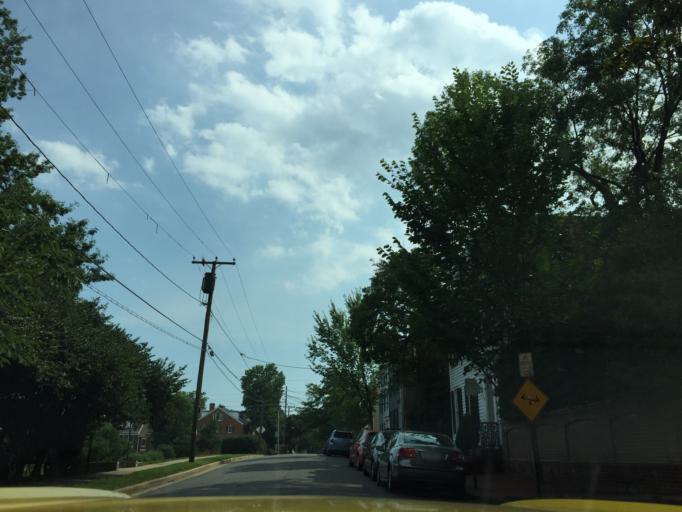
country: US
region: Virginia
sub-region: City of Alexandria
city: Alexandria
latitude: 38.7998
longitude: -77.0424
